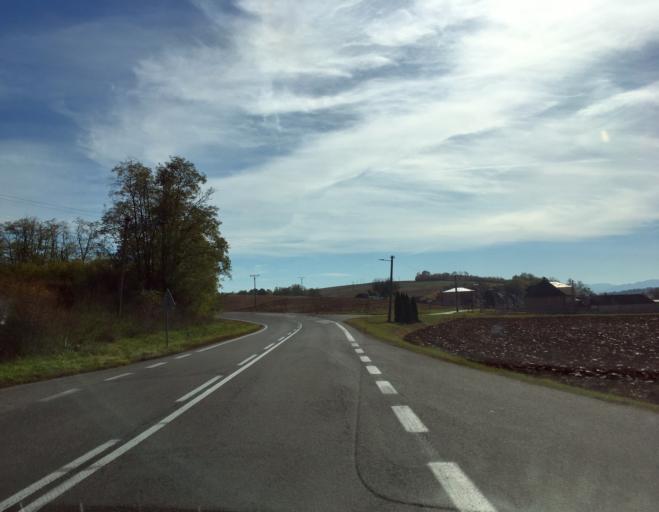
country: SK
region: Banskobystricky
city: Dudince
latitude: 48.1229
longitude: 18.8457
